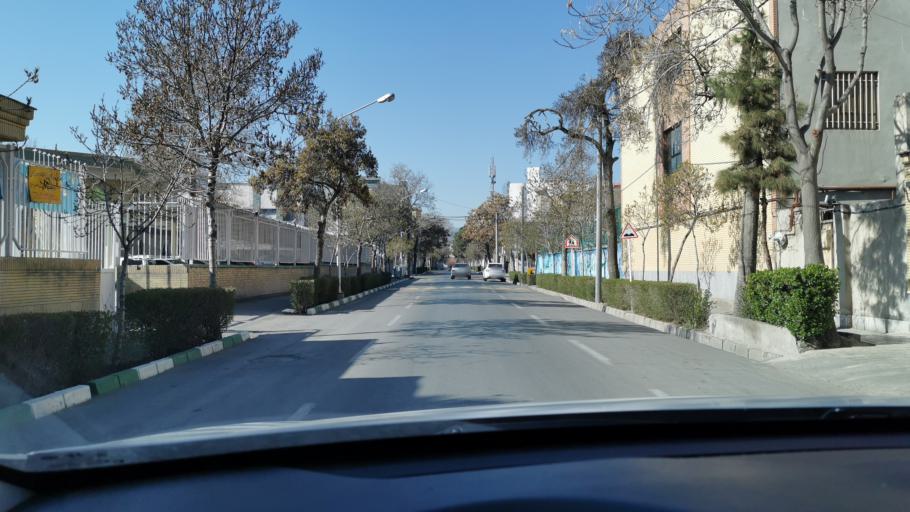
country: IR
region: Razavi Khorasan
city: Mashhad
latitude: 36.2890
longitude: 59.5870
